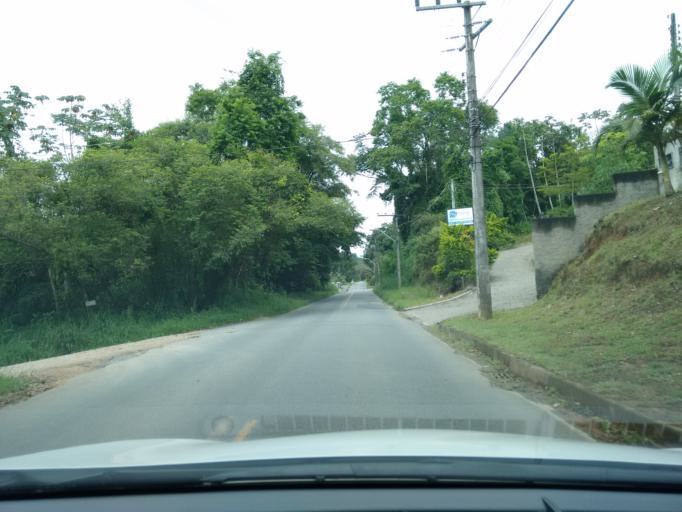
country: BR
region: Santa Catarina
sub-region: Blumenau
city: Blumenau
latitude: -26.8650
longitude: -49.1401
